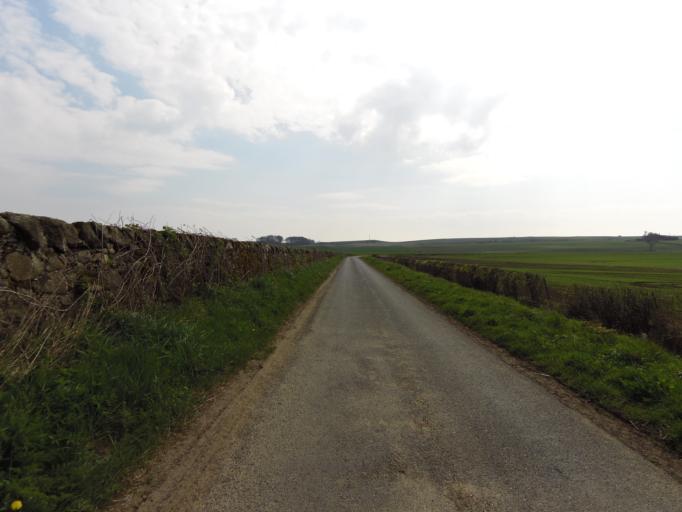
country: GB
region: Scotland
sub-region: Fife
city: Kinghorn
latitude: 56.0885
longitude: -3.1828
